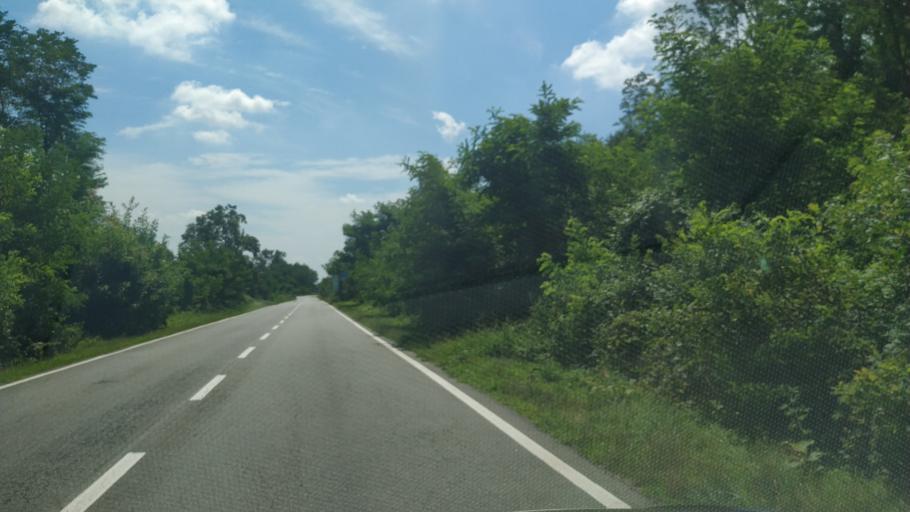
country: IT
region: Piedmont
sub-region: Provincia di Novara
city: Briga Novarese
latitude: 45.7094
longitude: 8.4445
